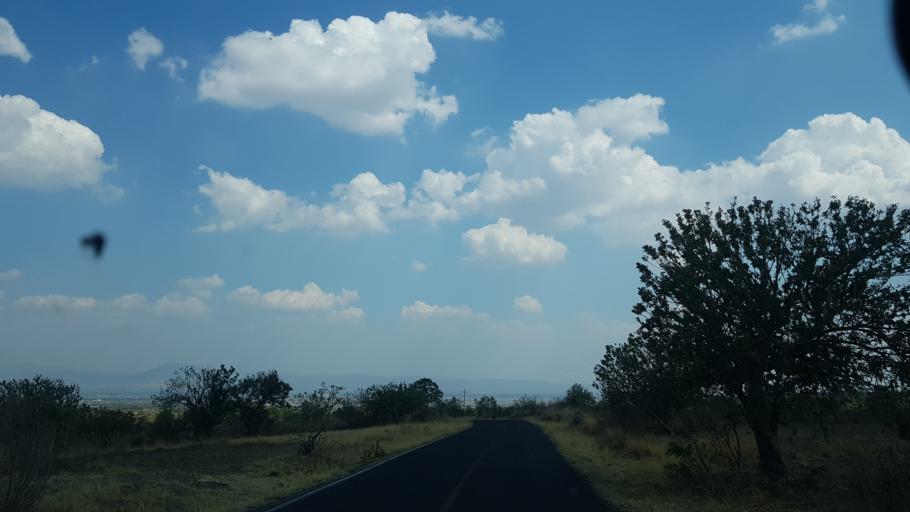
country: MX
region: Puebla
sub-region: Atlixco
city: San Pedro Benito Juarez
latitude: 18.9474
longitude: -98.5383
